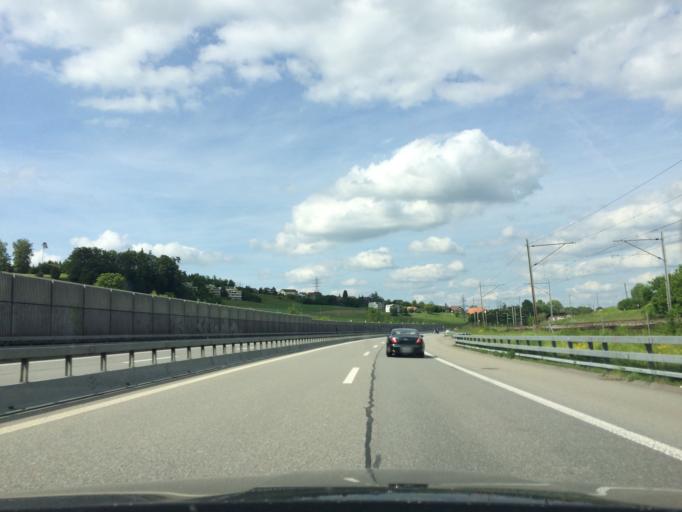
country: CH
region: Bern
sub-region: Bern-Mittelland District
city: Frauenkappelen
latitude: 46.9173
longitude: 7.3635
